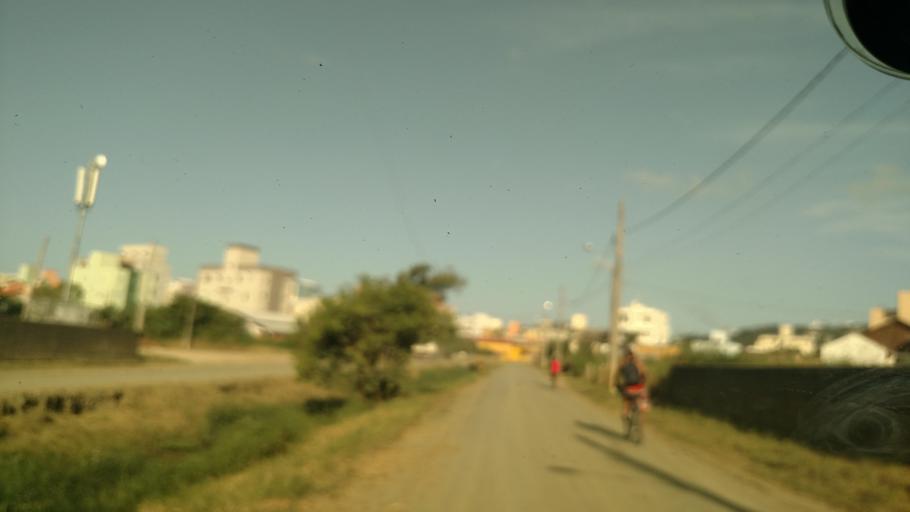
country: BR
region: Santa Catarina
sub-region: Porto Belo
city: Porto Belo
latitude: -27.1449
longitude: -48.5100
